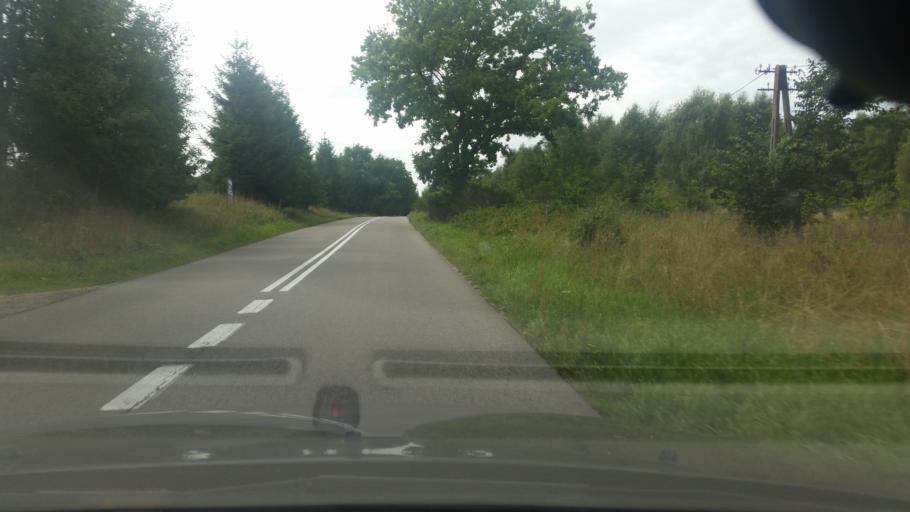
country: PL
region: Pomeranian Voivodeship
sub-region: Powiat leborski
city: Leba
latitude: 54.7453
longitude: 17.6590
